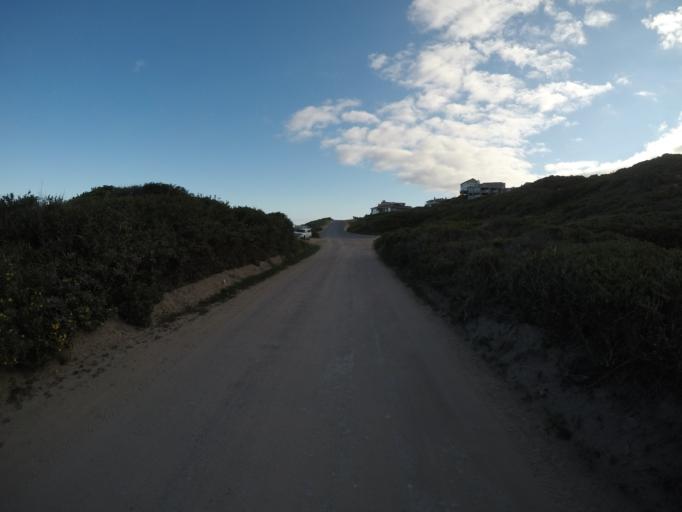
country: ZA
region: Western Cape
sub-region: Eden District Municipality
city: Riversdale
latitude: -34.4196
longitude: 21.3510
